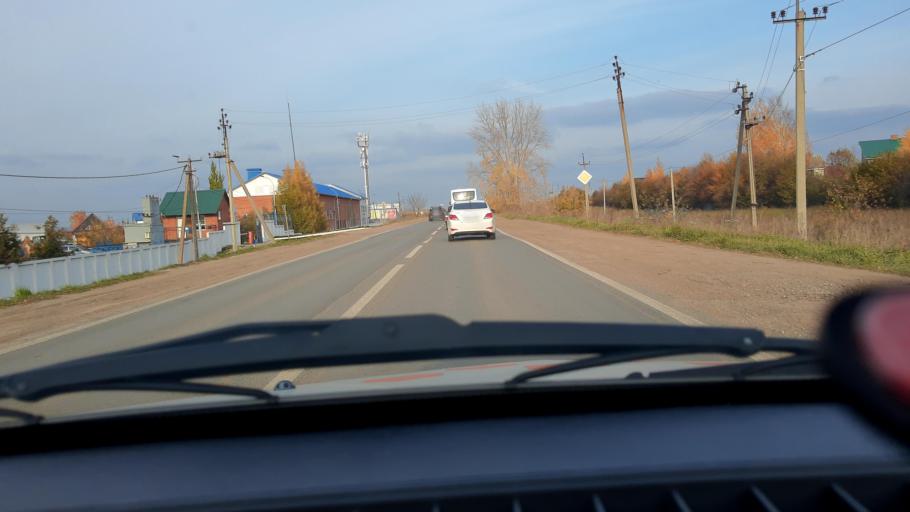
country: RU
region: Bashkortostan
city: Iglino
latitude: 54.7938
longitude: 56.2436
